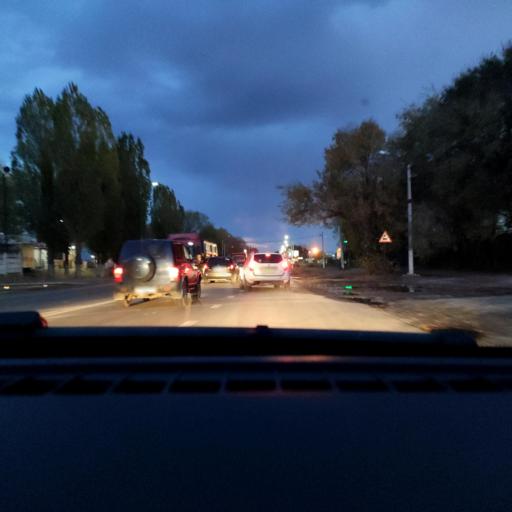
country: RU
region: Voronezj
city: Maslovka
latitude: 51.6456
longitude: 39.2974
